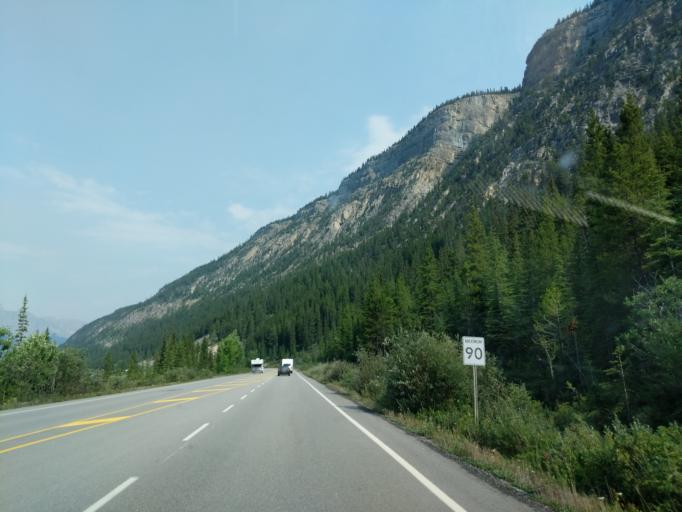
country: CA
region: Alberta
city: Lake Louise
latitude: 51.8461
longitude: -116.6224
